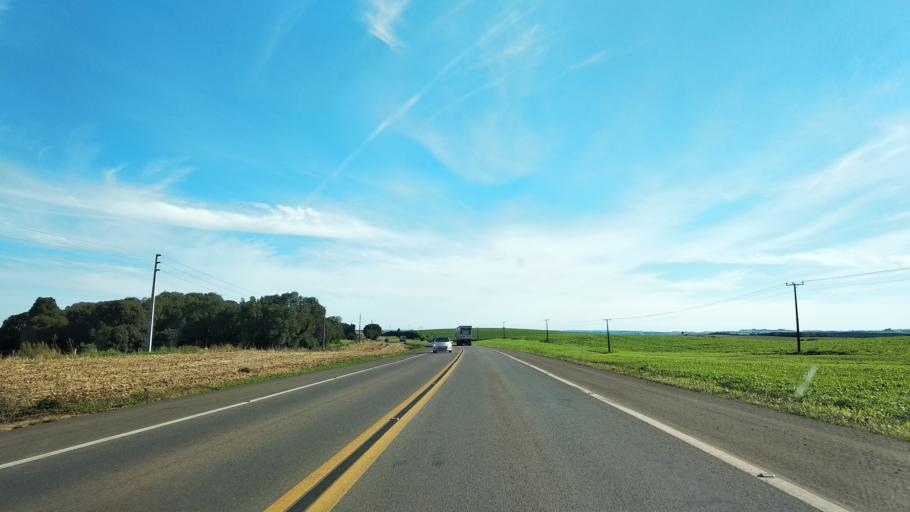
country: BR
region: Santa Catarina
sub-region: Campos Novos
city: Campos Novos
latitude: -27.4910
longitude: -51.3310
